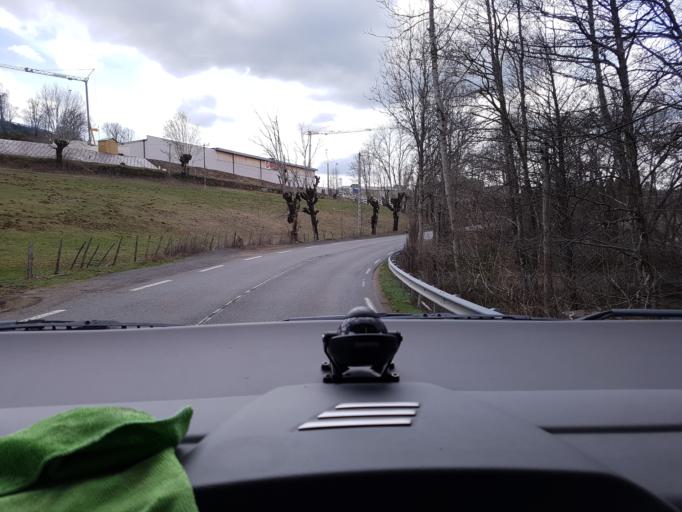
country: FR
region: Midi-Pyrenees
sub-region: Departement de l'Aveyron
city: Laguiole
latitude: 44.6877
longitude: 2.8537
